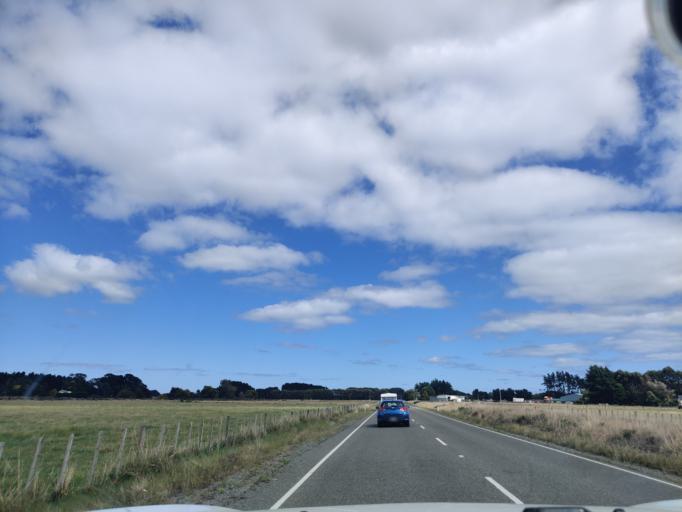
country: NZ
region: Manawatu-Wanganui
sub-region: Horowhenua District
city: Foxton
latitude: -40.4185
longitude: 175.4214
